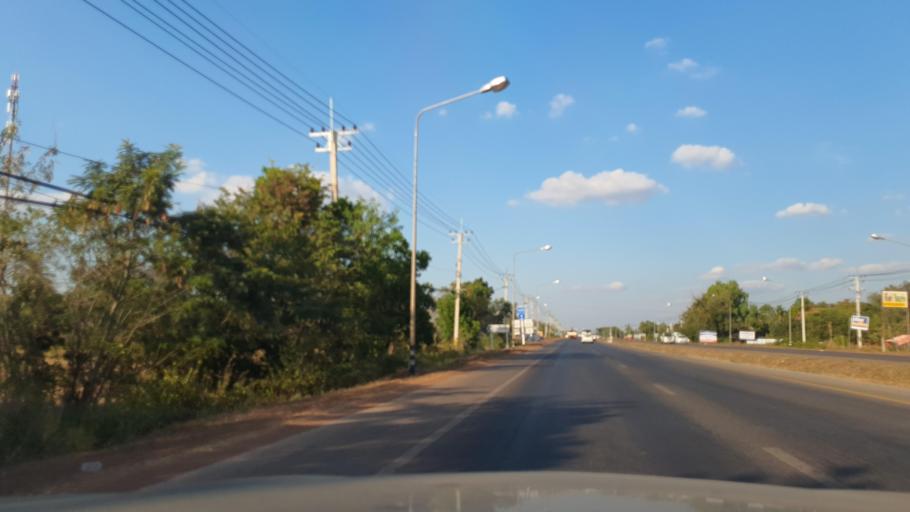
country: TH
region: Sakon Nakhon
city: Sakon Nakhon
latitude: 17.2366
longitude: 104.1092
